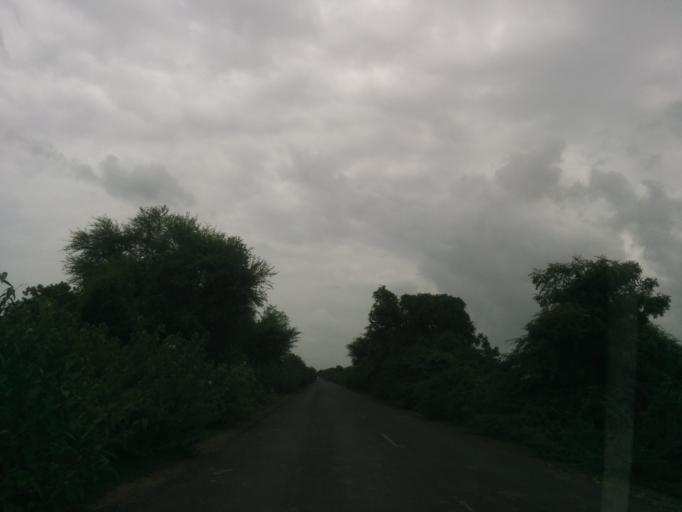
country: IN
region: Gujarat
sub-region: Ahmadabad
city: Sanand
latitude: 23.0703
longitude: 72.3945
